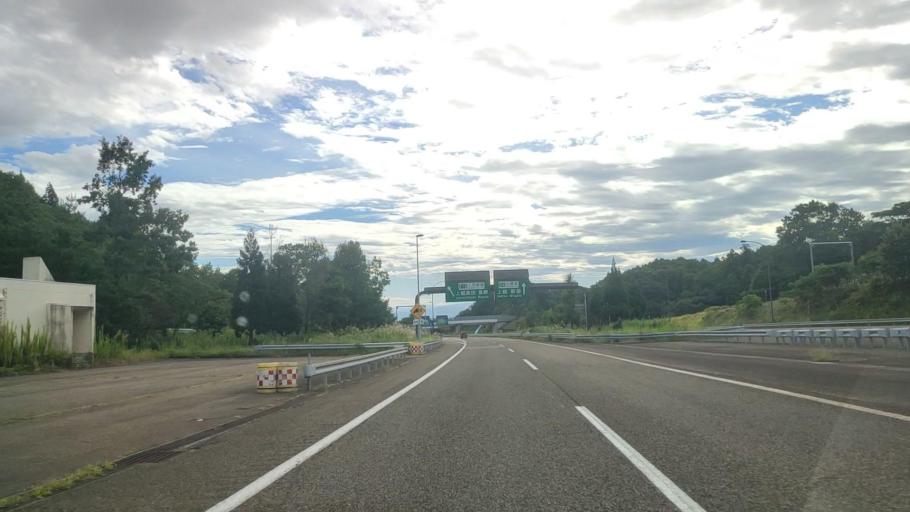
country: JP
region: Niigata
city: Joetsu
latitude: 37.1414
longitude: 138.2098
